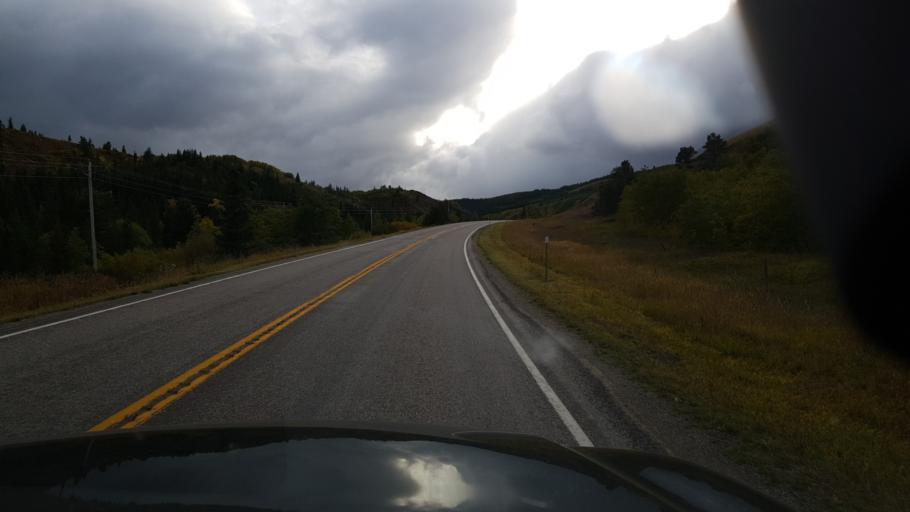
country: US
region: Montana
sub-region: Glacier County
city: South Browning
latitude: 48.3484
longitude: -113.3088
